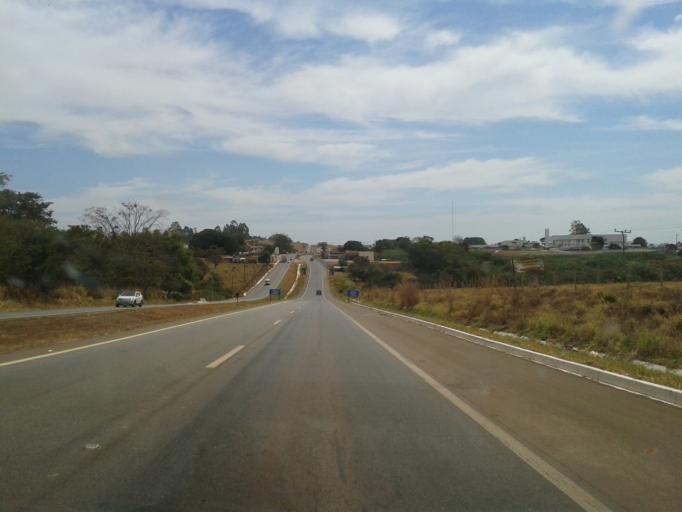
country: BR
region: Goias
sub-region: Itaberai
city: Itaberai
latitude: -16.1318
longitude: -49.6467
